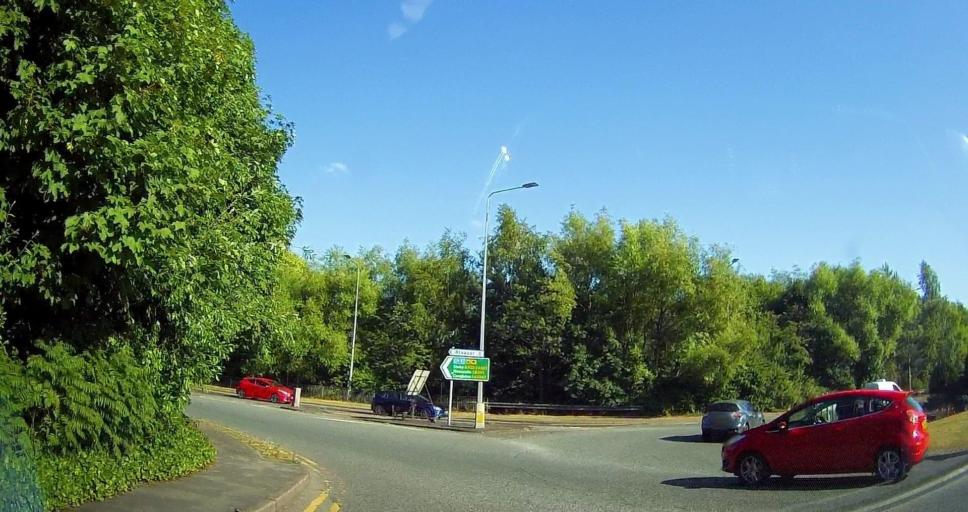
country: GB
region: England
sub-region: Cheshire East
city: Sandbach
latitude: 53.1414
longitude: -2.3612
